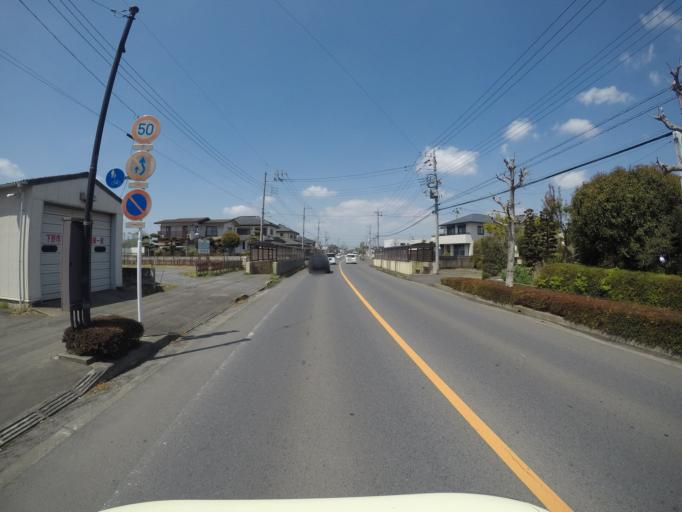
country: JP
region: Tochigi
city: Mibu
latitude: 36.3813
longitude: 139.8407
